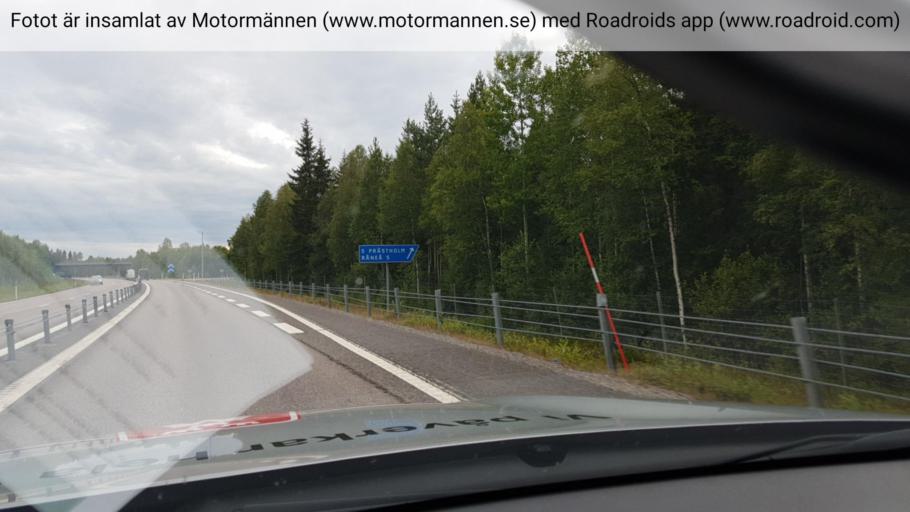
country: SE
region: Norrbotten
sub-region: Lulea Kommun
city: Ranea
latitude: 65.8424
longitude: 22.2671
